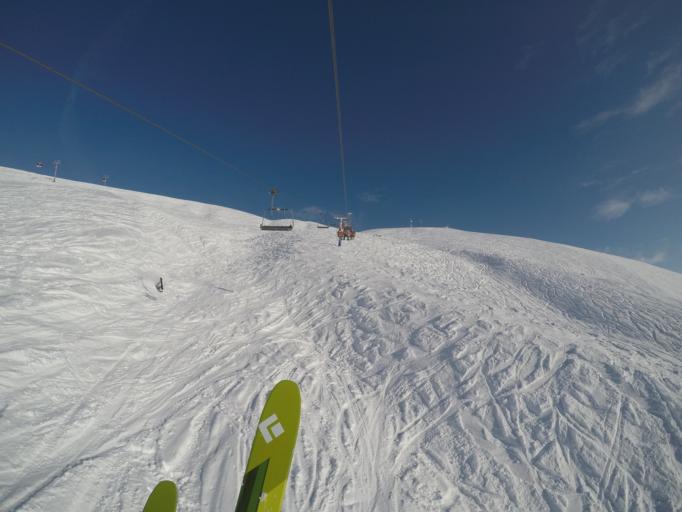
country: GE
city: Gudauri
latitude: 42.4840
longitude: 44.4955
